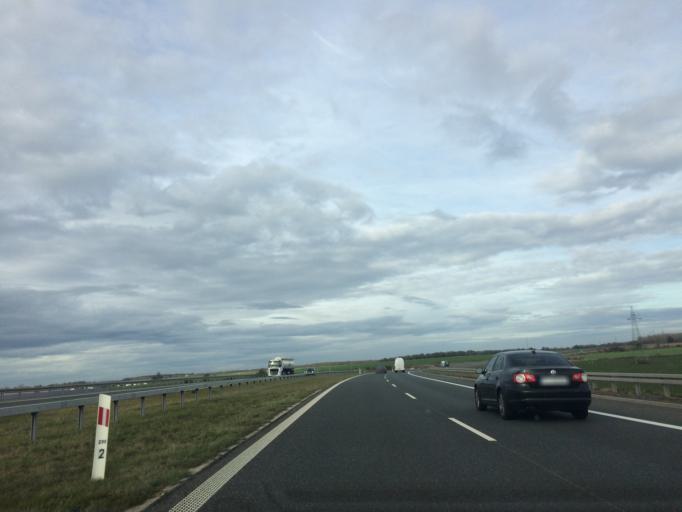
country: PL
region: Lower Silesian Voivodeship
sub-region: Powiat legnicki
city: Milkowice
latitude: 51.1832
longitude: 16.0867
